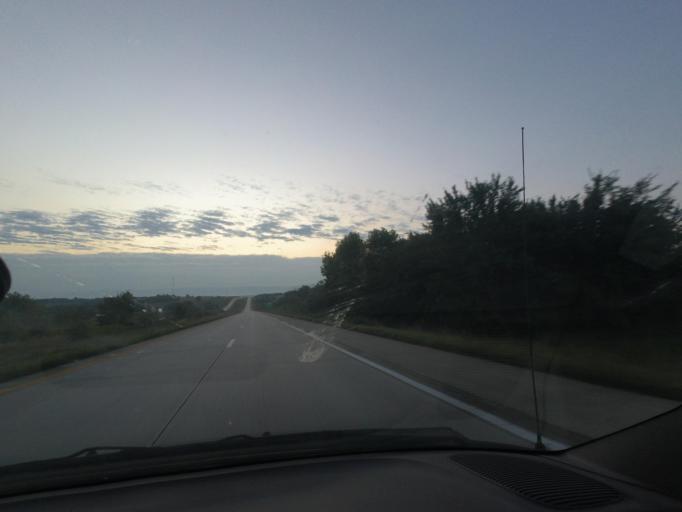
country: US
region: Missouri
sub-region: Linn County
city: Marceline
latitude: 39.7649
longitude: -92.7682
